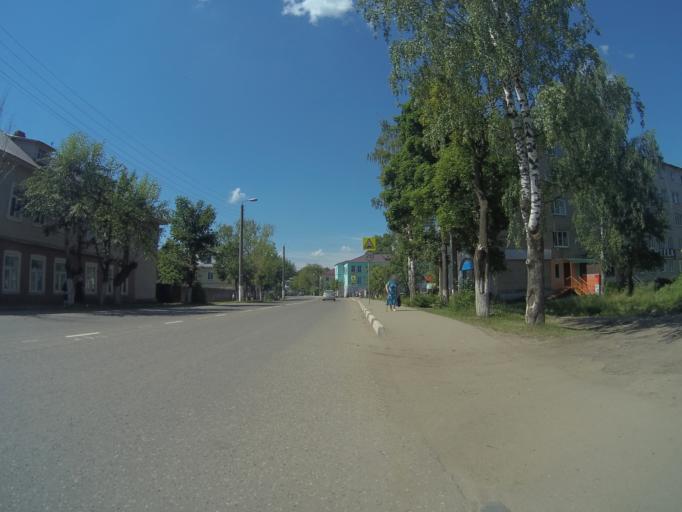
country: RU
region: Ivanovo
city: Privolzhsk
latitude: 57.3794
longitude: 41.2899
